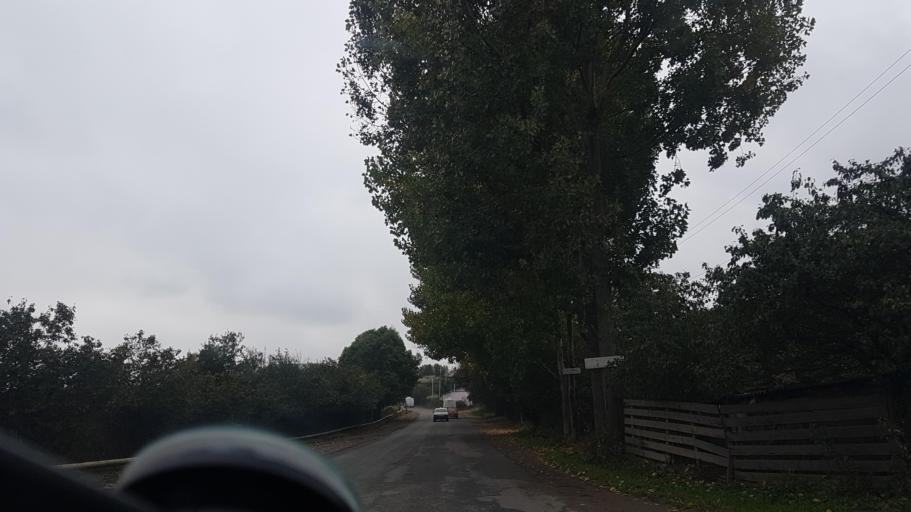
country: AZ
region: Gadabay Rayon
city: Ariqdam
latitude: 40.6559
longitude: 45.8064
